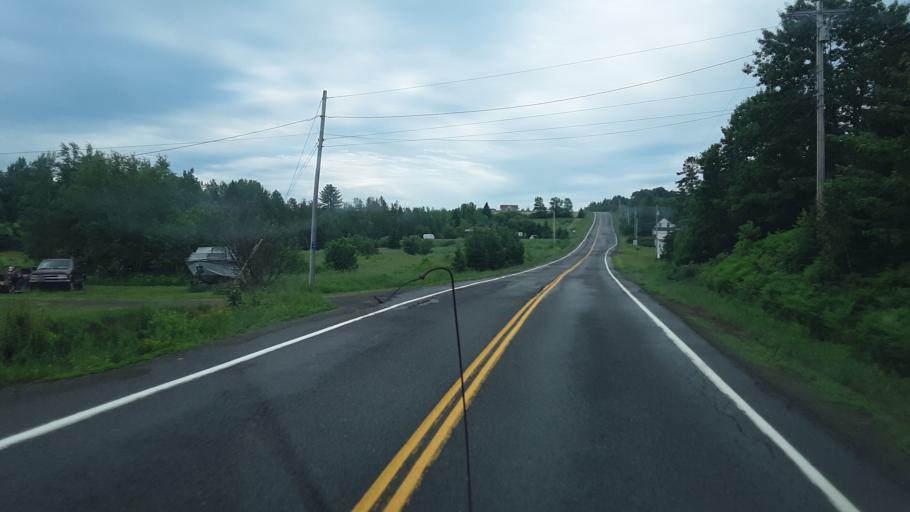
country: US
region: Maine
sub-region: Penobscot County
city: Patten
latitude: 46.0528
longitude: -68.4421
